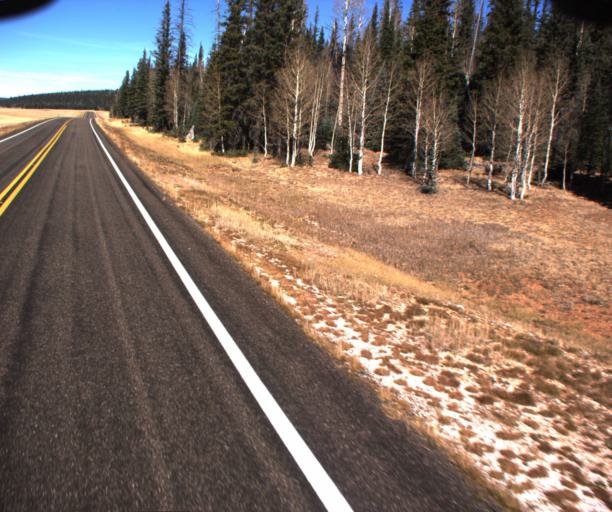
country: US
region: Arizona
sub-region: Coconino County
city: Grand Canyon
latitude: 36.3495
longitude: -112.1178
